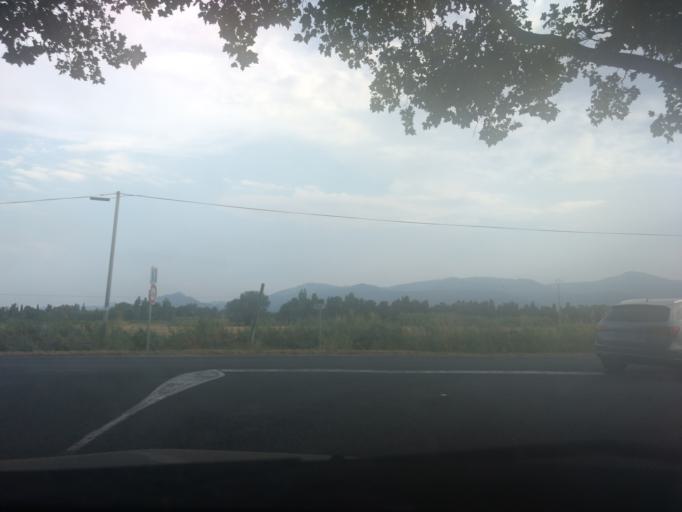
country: FR
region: Languedoc-Roussillon
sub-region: Departement des Pyrenees-Orientales
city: Latour-Bas-Elne
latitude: 42.5965
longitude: 3.0324
